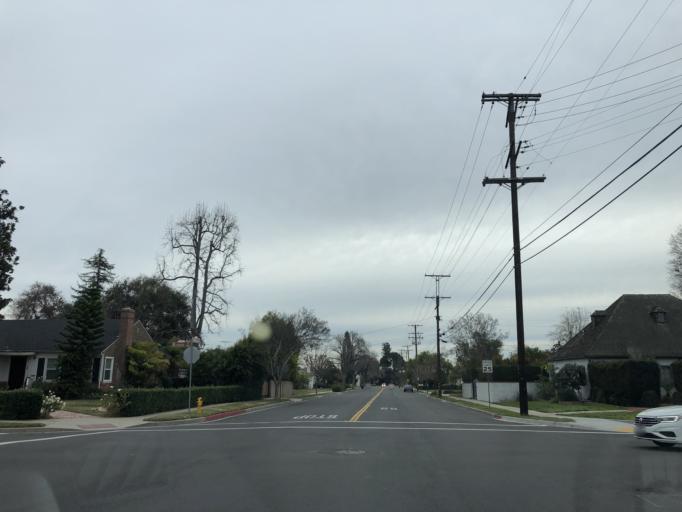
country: US
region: California
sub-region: Los Angeles County
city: San Marino
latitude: 34.1100
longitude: -118.1042
